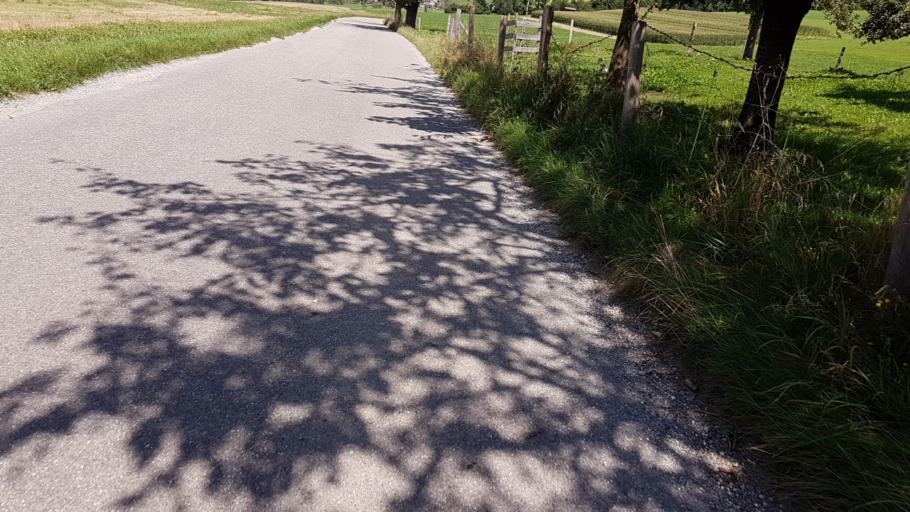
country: CH
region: Lucerne
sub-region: Entlebuch District
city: Oberdiessbach
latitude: 46.8569
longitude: 7.6245
